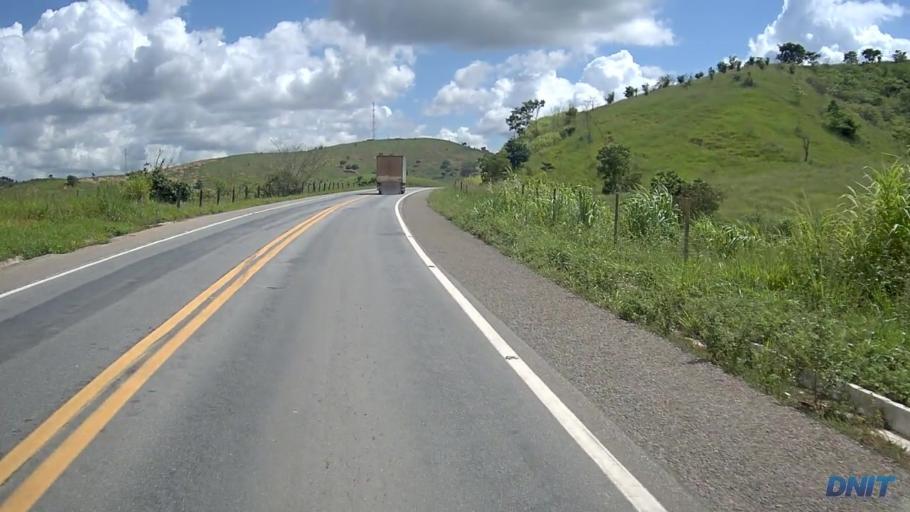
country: BR
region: Minas Gerais
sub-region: Governador Valadares
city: Governador Valadares
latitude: -19.0321
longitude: -42.1487
